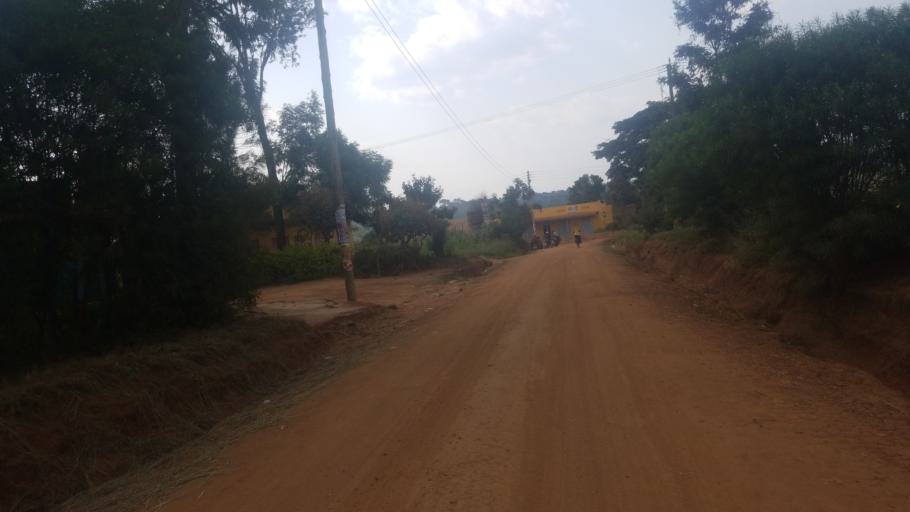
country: UG
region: Central Region
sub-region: Sembabule District
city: Sembabule
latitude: -0.0808
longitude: 31.4574
